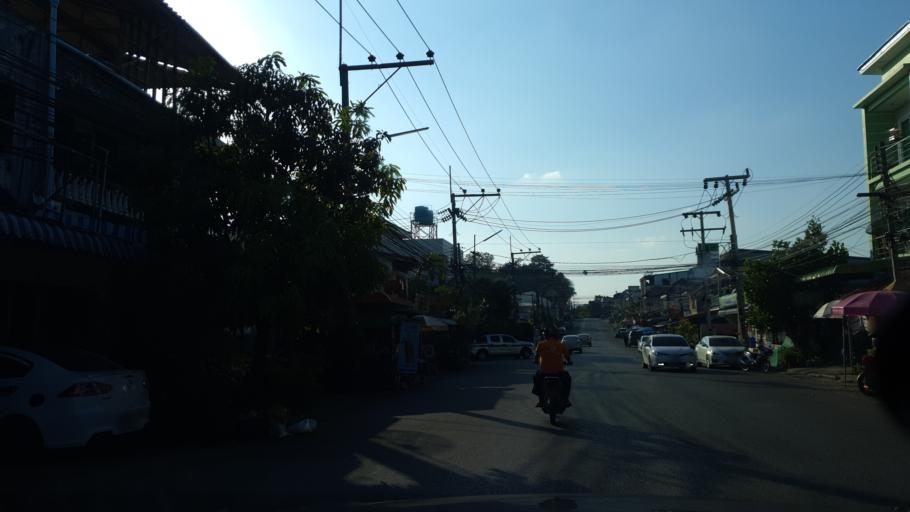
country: TH
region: Krabi
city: Krabi
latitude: 8.0806
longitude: 98.9134
